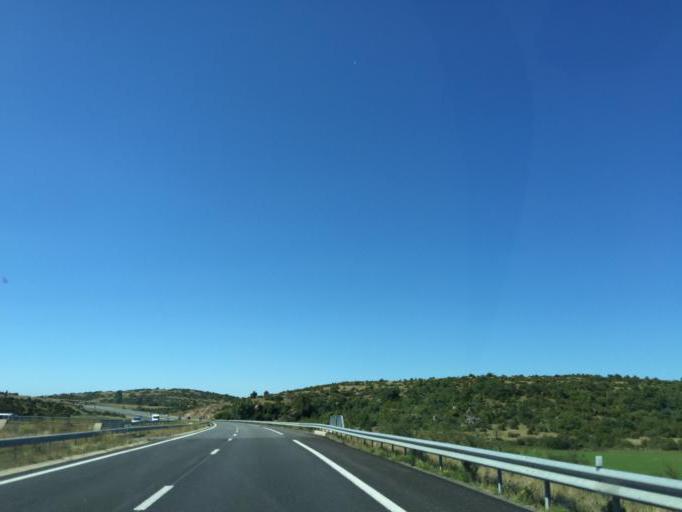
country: FR
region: Midi-Pyrenees
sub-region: Departement de l'Aveyron
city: La Cavalerie
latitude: 43.9027
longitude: 3.2773
